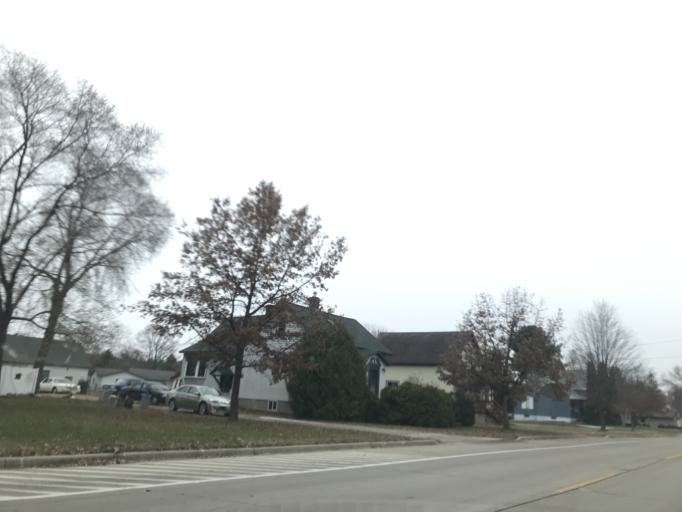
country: US
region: Wisconsin
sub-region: Marinette County
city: Marinette
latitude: 45.0781
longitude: -87.6194
